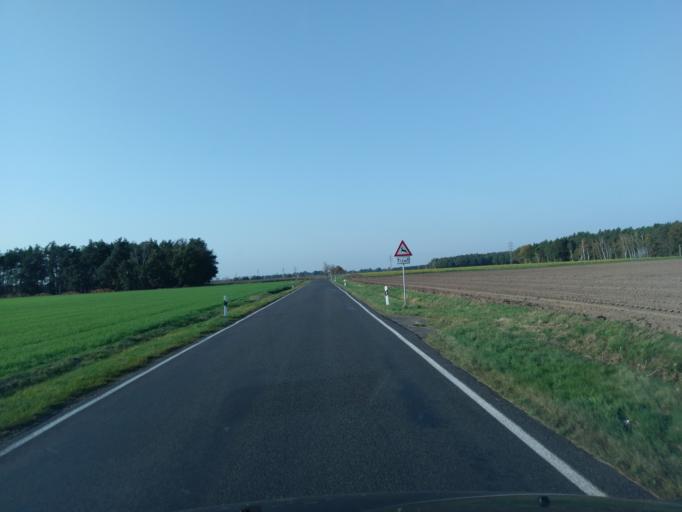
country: DE
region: Brandenburg
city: Falkenberg
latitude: 51.5512
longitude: 13.2704
